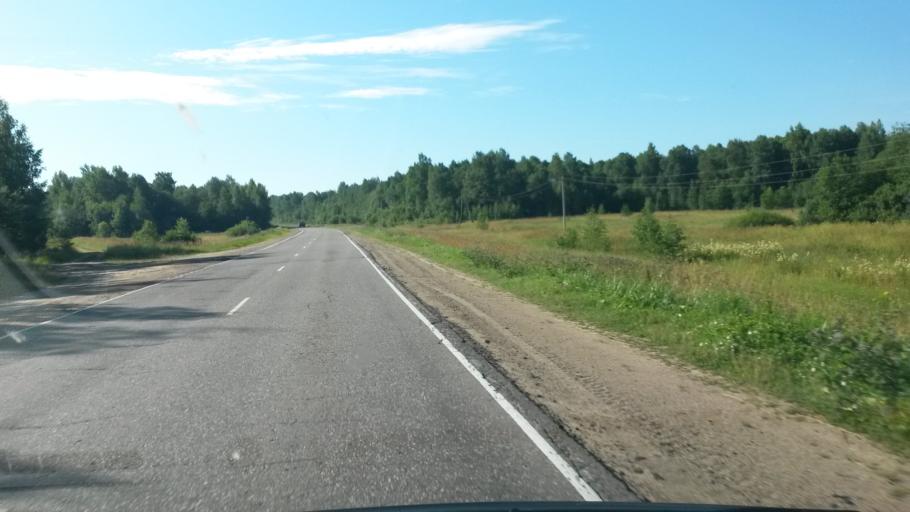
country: RU
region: Ivanovo
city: Pistsovo
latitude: 57.1421
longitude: 40.5752
